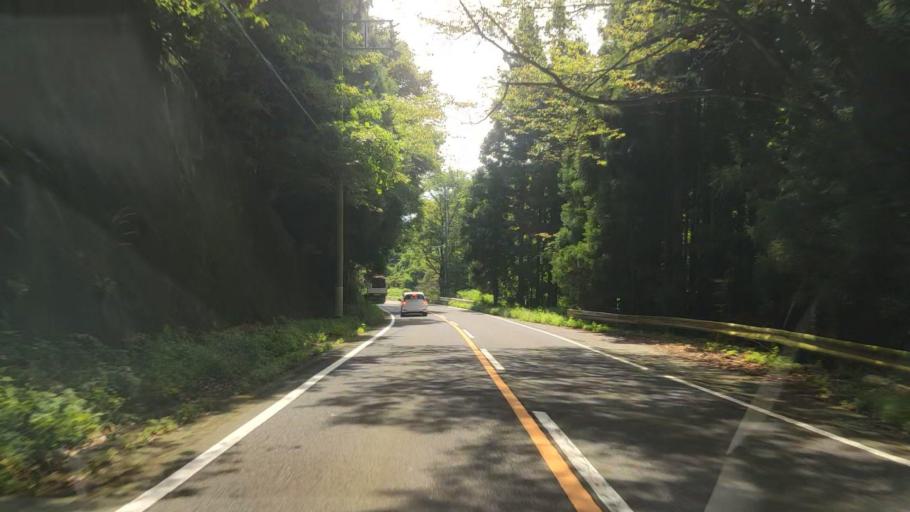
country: JP
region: Gunma
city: Numata
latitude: 36.6326
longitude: 138.9932
